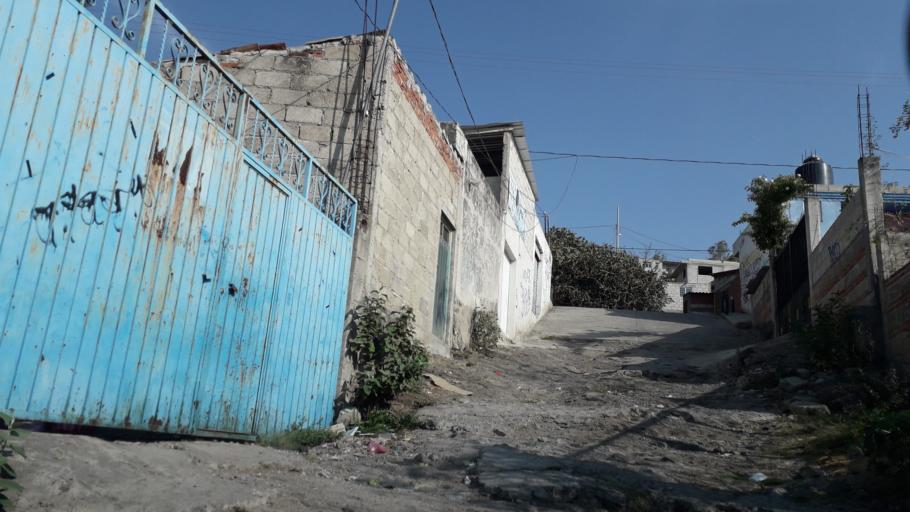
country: MX
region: Puebla
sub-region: Puebla
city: San Andres Azumiatla
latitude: 18.9035
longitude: -98.2542
